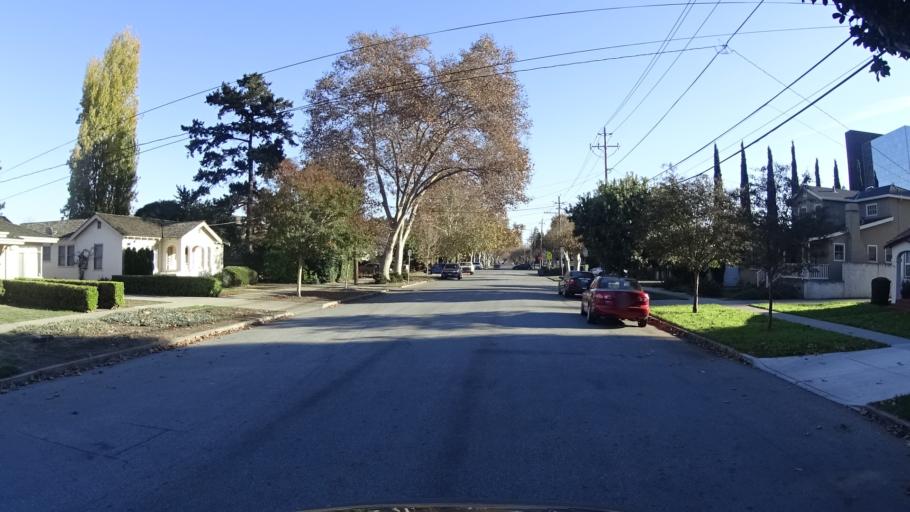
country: US
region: California
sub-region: Santa Clara County
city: San Jose
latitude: 37.3546
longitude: -121.9030
